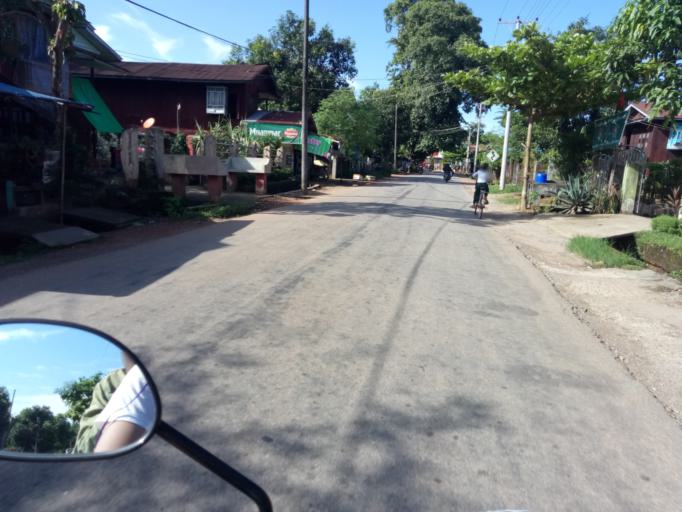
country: MM
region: Mon
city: Mawlamyine
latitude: 16.3871
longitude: 97.5499
